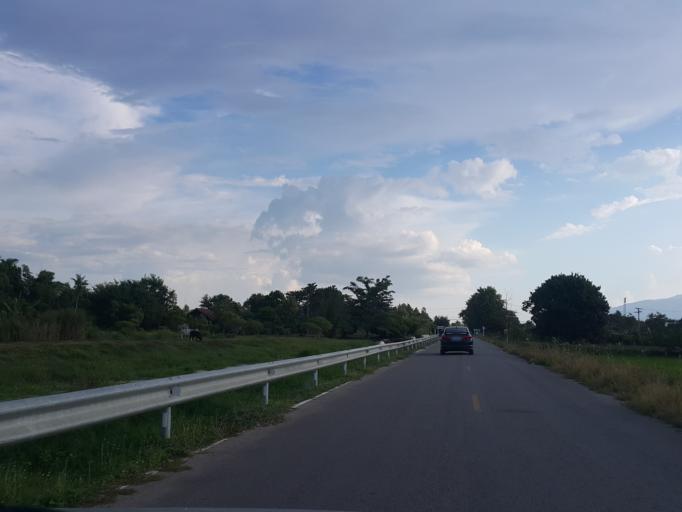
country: TH
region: Chiang Mai
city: Mae Taeng
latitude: 18.9962
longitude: 98.9813
